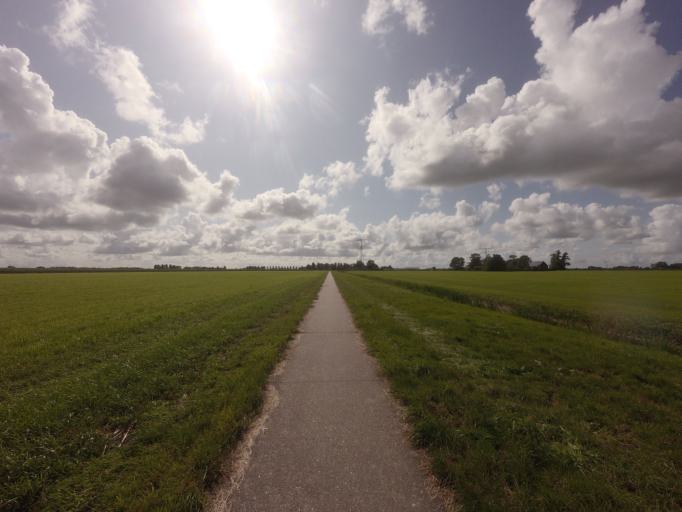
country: NL
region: Friesland
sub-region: Sudwest Fryslan
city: Sneek
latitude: 53.0649
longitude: 5.6362
